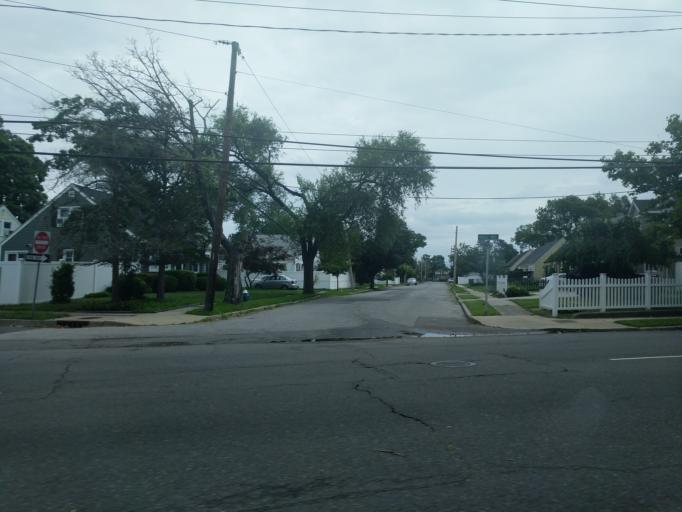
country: US
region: New York
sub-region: Nassau County
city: Hewlett
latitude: 40.6466
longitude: -73.7063
